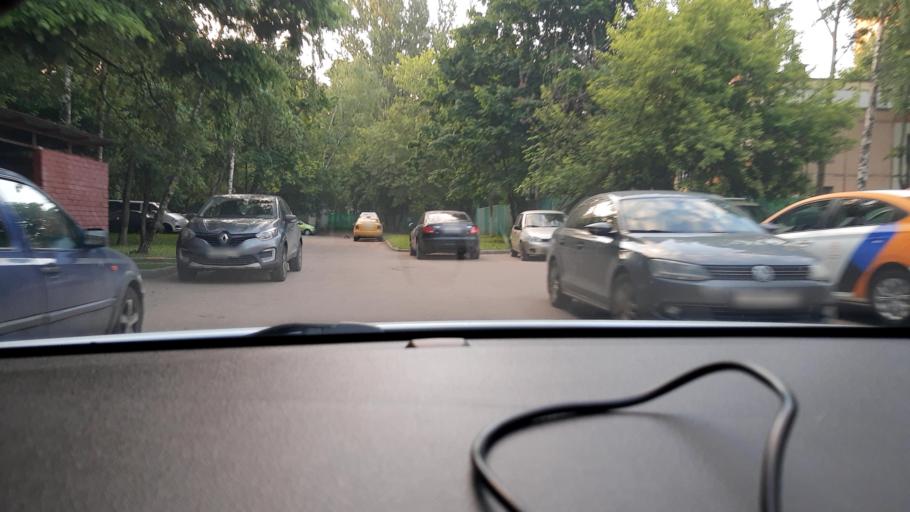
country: RU
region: Moscow
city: Tsaritsyno
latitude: 55.6263
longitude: 37.6484
